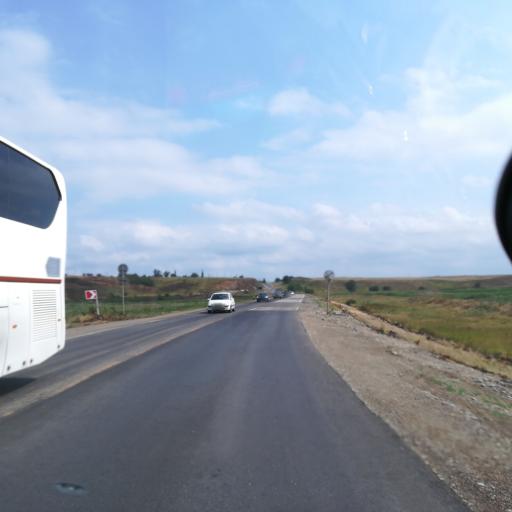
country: RU
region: Krasnodarskiy
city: Varenikovskaya
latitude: 45.1775
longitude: 37.6529
